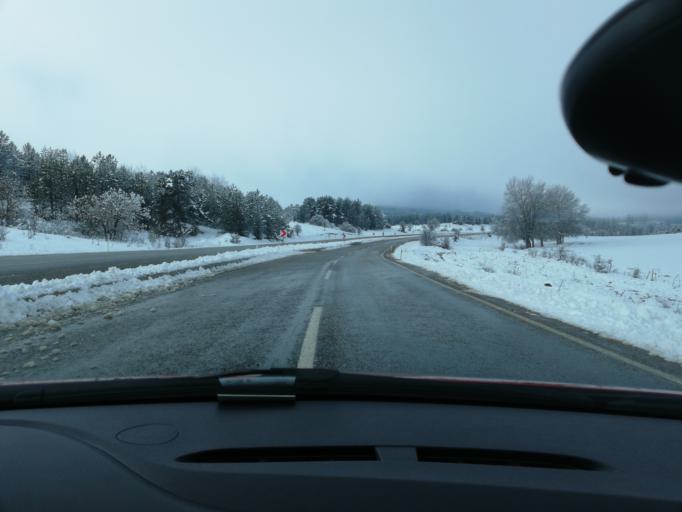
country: TR
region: Kastamonu
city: Ihsangazi
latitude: 41.3054
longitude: 33.5693
